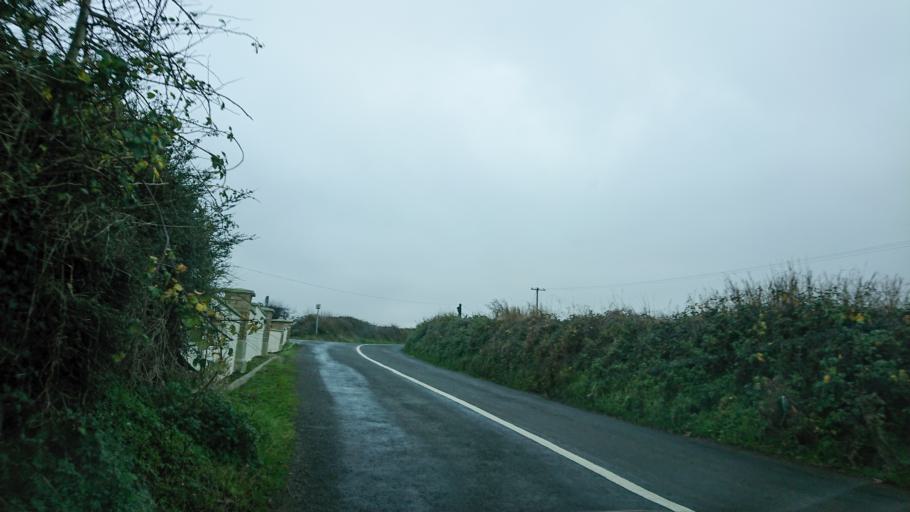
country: IE
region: Munster
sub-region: Waterford
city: Dunmore East
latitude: 52.1597
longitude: -7.0628
